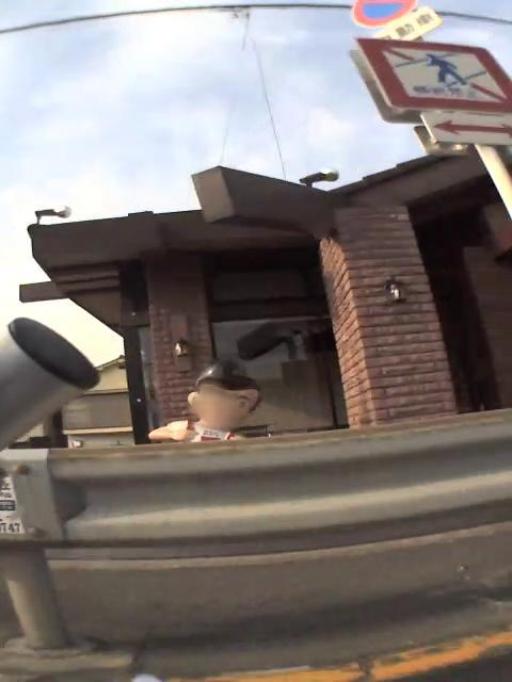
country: JP
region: Osaka
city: Neyagawa
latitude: 34.7398
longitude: 135.6368
